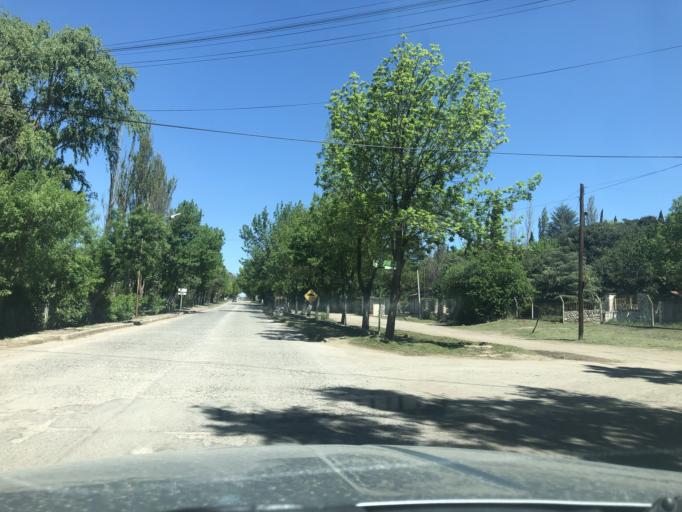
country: AR
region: Cordoba
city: La Granja
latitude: -31.0206
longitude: -64.2743
